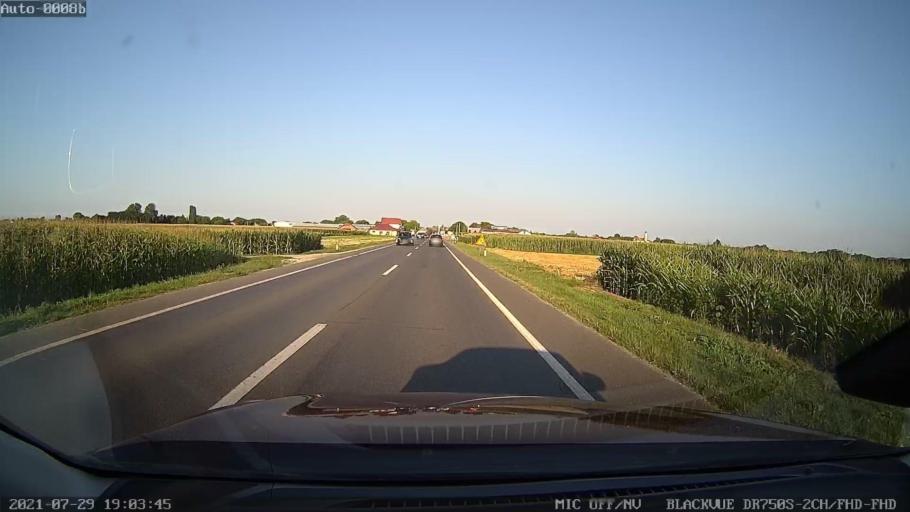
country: HR
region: Medimurska
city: Kursanec
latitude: 46.2974
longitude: 16.4274
